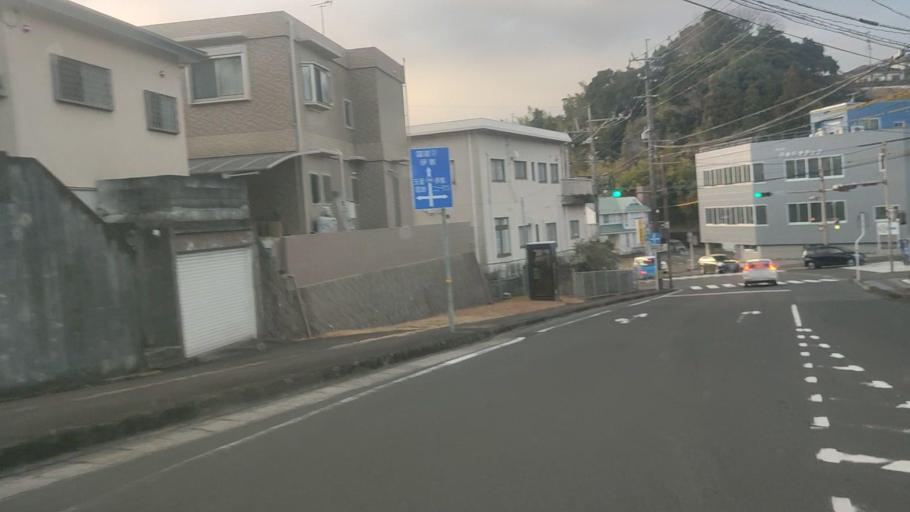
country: JP
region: Kagoshima
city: Kagoshima-shi
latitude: 31.6269
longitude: 130.5470
